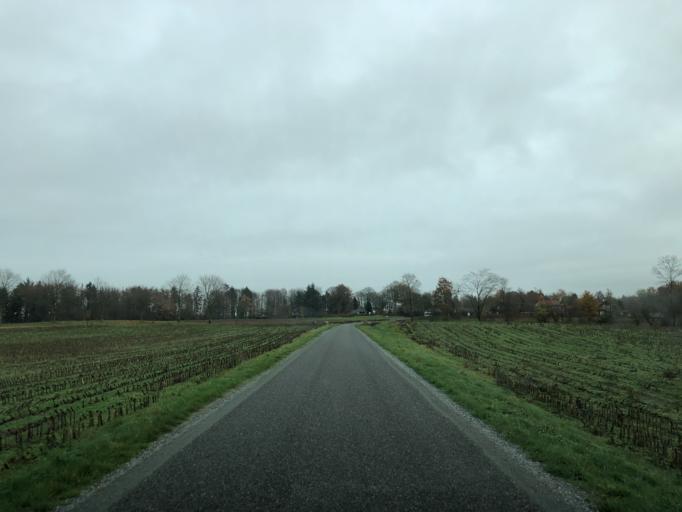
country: DK
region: Central Jutland
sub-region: Silkeborg Kommune
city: Virklund
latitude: 56.0395
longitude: 9.4391
